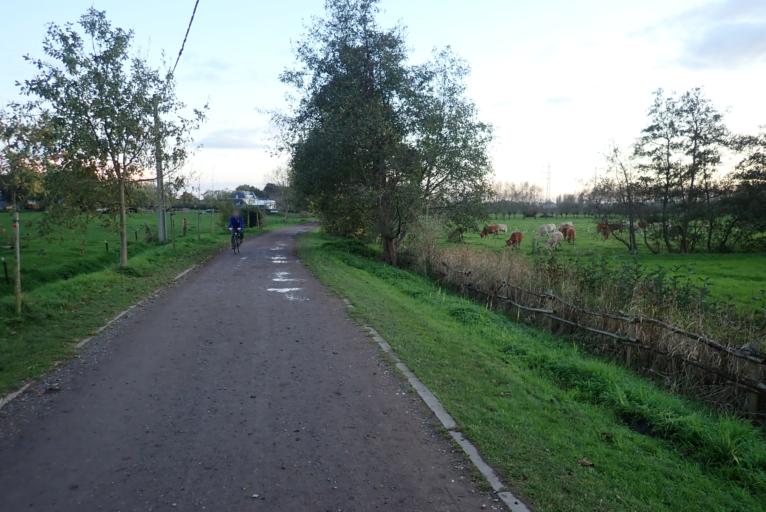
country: BE
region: Flanders
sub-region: Provincie Antwerpen
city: Niel
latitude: 51.1126
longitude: 4.3179
